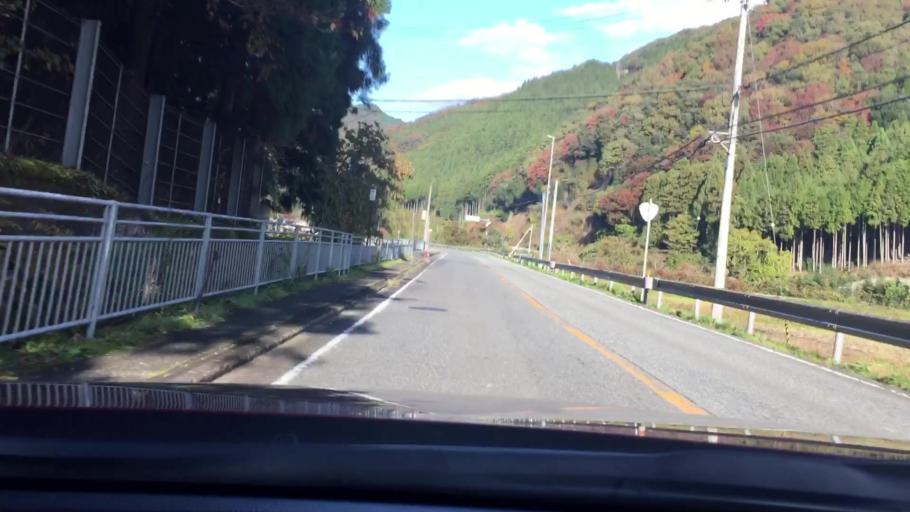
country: JP
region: Hyogo
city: Yamazakicho-nakabirose
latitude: 35.1394
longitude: 134.5547
